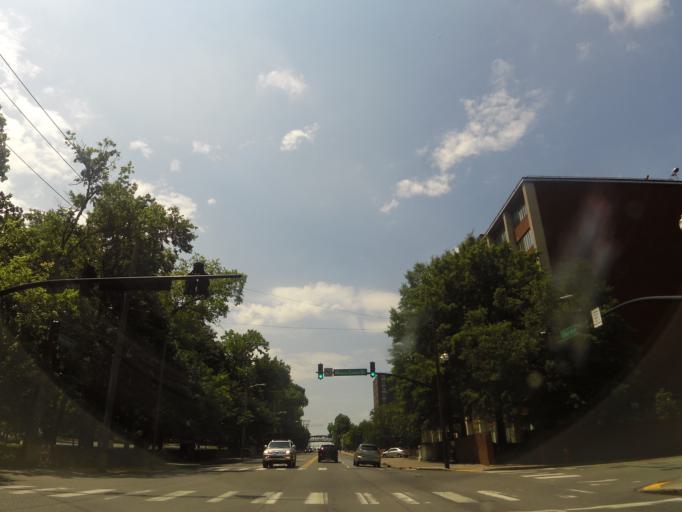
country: US
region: Tennessee
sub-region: Davidson County
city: Nashville
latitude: 36.1431
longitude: -86.8000
